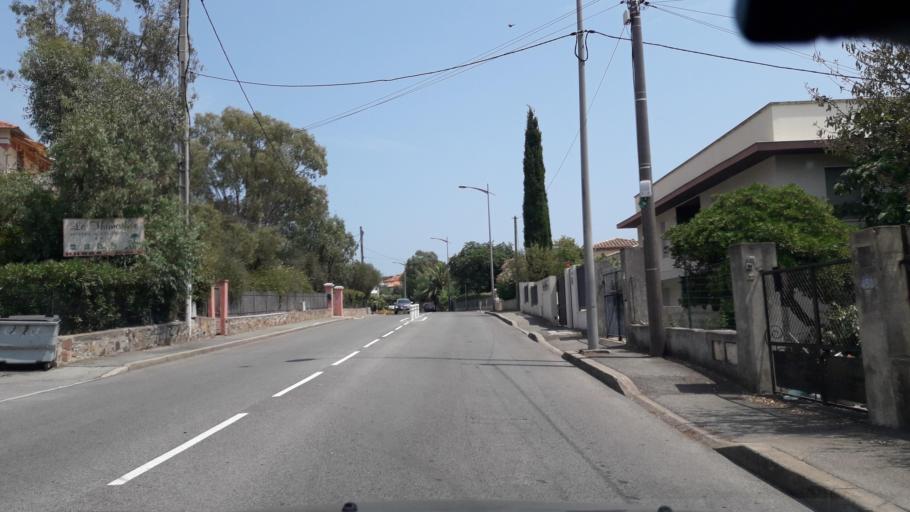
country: FR
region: Provence-Alpes-Cote d'Azur
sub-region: Departement du Var
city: Saint-Raphael
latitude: 43.4203
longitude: 6.7850
